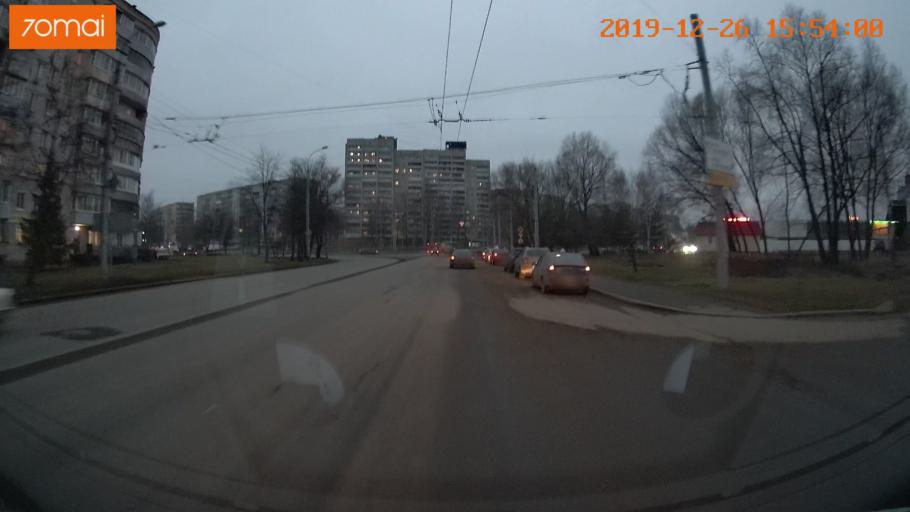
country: RU
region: Jaroslavl
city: Rybinsk
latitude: 58.0471
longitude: 38.8218
